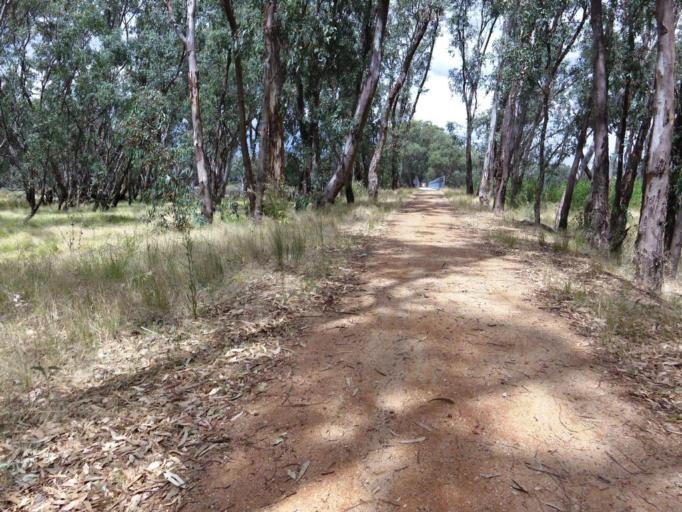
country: AU
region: Victoria
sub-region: Greater Bendigo
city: Kennington
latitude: -36.8715
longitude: 144.6279
